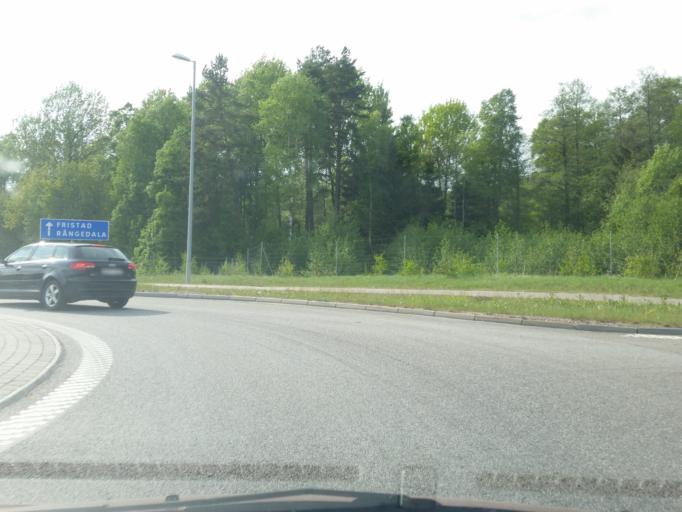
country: SE
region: Vaestra Goetaland
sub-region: Boras Kommun
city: Dalsjofors
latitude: 57.7993
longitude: 13.1558
